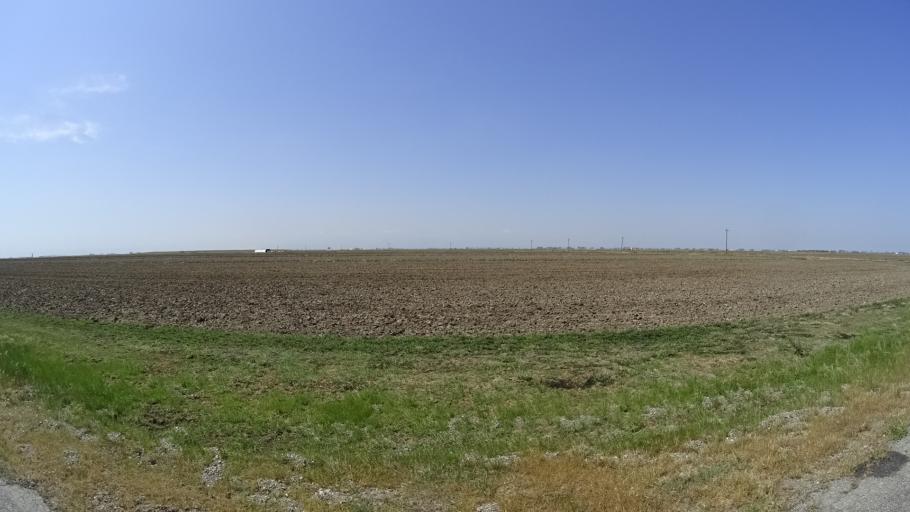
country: US
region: California
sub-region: Glenn County
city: Willows
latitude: 39.5279
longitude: -122.0326
